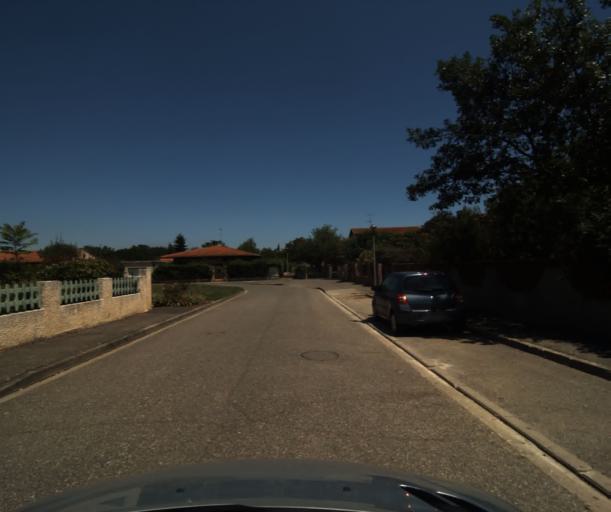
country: FR
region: Midi-Pyrenees
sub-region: Departement de la Haute-Garonne
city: Roquettes
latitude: 43.4943
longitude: 1.3740
